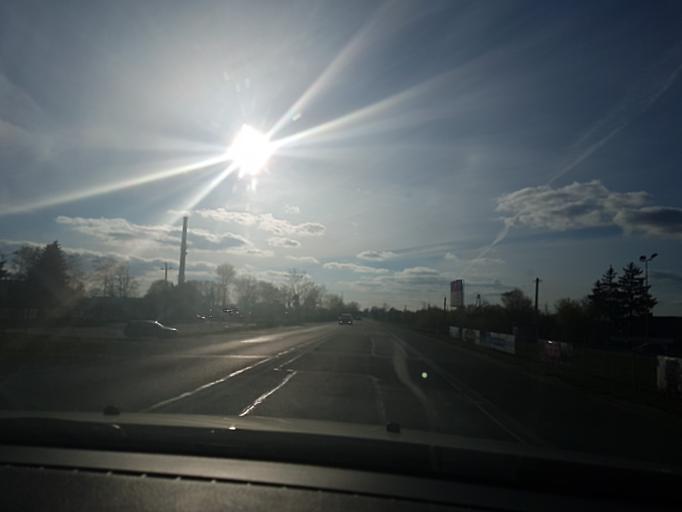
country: PL
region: Lodz Voivodeship
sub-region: Powiat kutnowski
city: Krzyzanow
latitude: 52.2241
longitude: 19.4191
